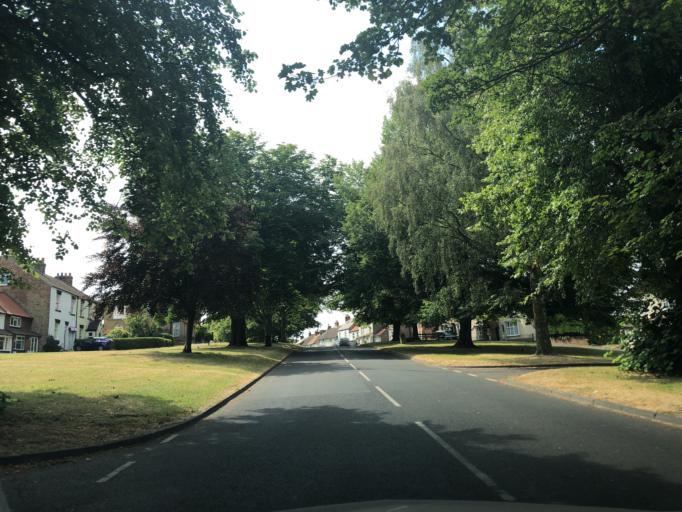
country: GB
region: England
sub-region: Redcar and Cleveland
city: Thornaby-on-Tees
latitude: 54.4507
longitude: -1.2771
